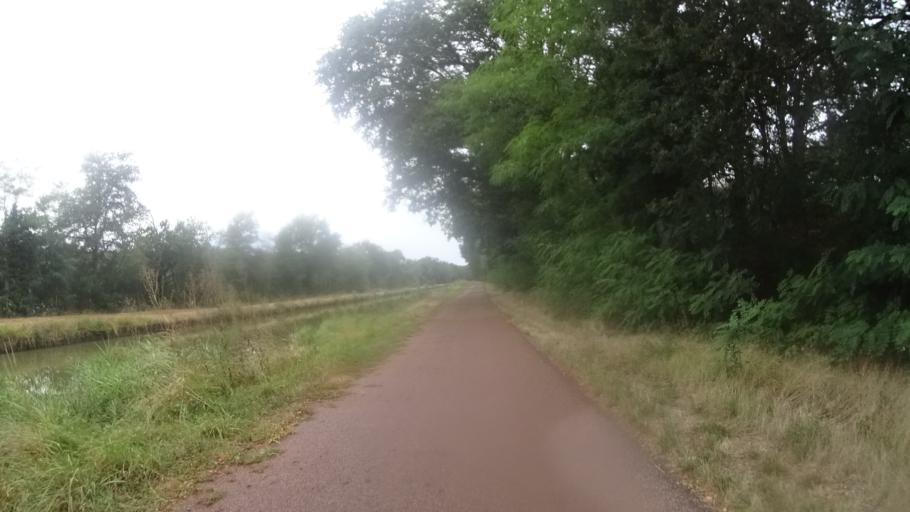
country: FR
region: Bourgogne
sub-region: Departement de la Nievre
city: Imphy
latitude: 46.8757
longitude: 3.2667
